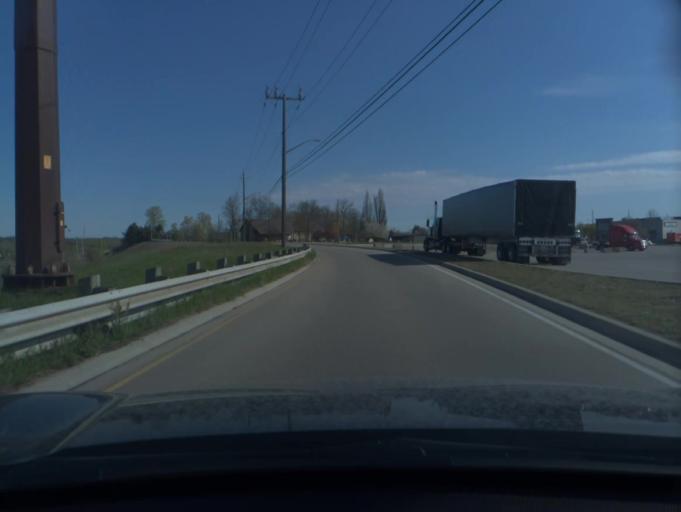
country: CA
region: Ontario
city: North Perth
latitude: 43.8351
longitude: -80.9999
